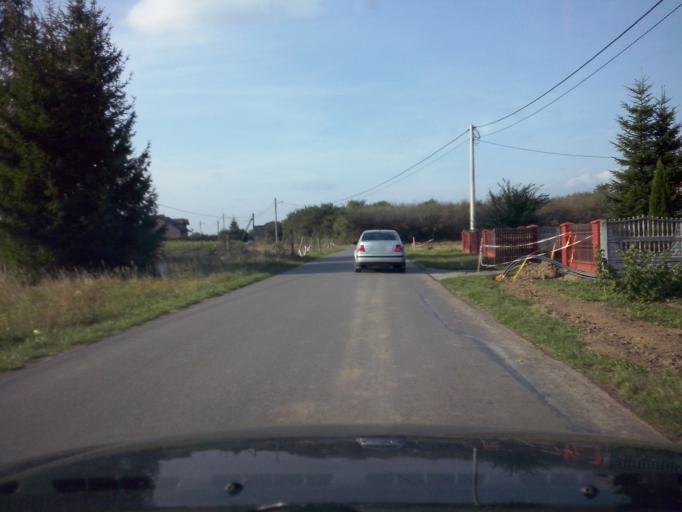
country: PL
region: Subcarpathian Voivodeship
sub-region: Powiat nizanski
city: Krzeszow
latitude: 50.3948
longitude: 22.3217
